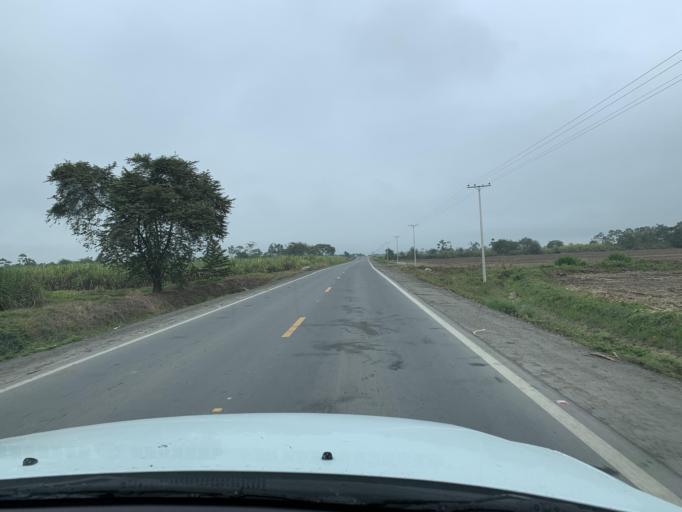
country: EC
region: Guayas
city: Coronel Marcelino Mariduena
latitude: -2.3097
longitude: -79.5102
